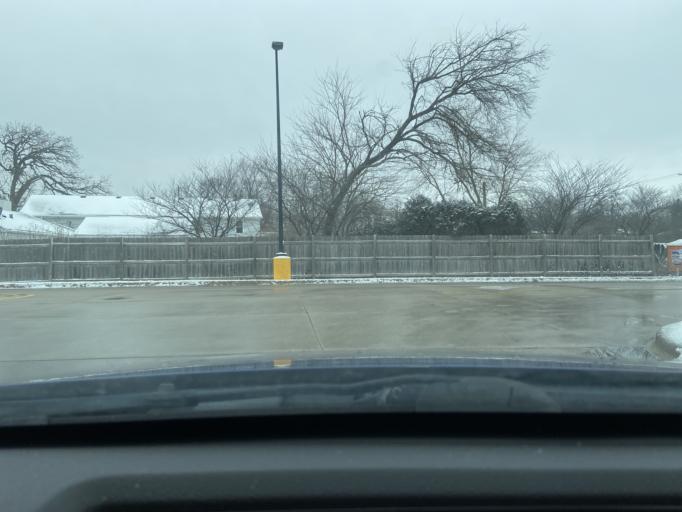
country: US
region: Illinois
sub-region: Lake County
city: Venetian Village
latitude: 42.3981
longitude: -88.0669
